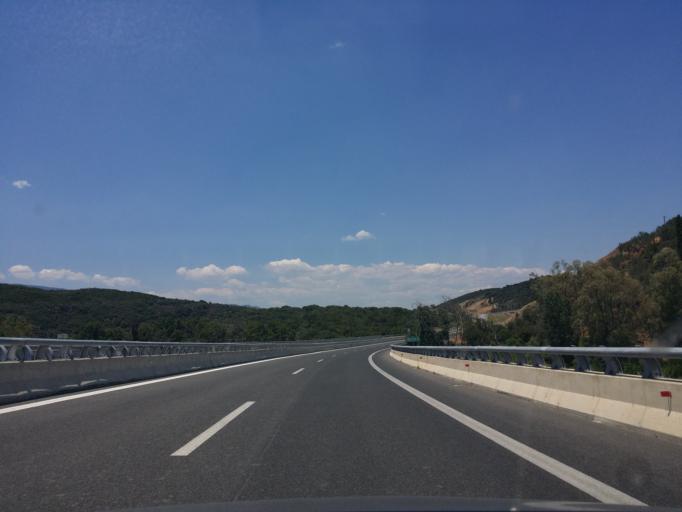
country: GR
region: Peloponnese
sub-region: Nomos Lakonias
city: Magoula
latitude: 37.1294
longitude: 22.4013
